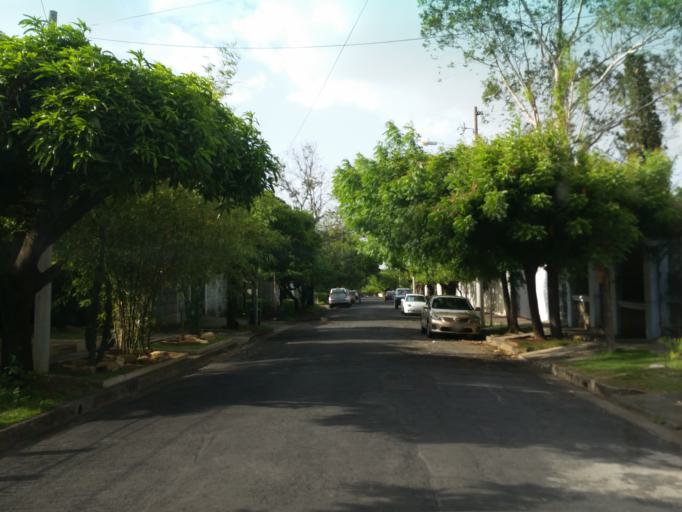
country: NI
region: Managua
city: Managua
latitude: 12.1209
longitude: -86.2559
